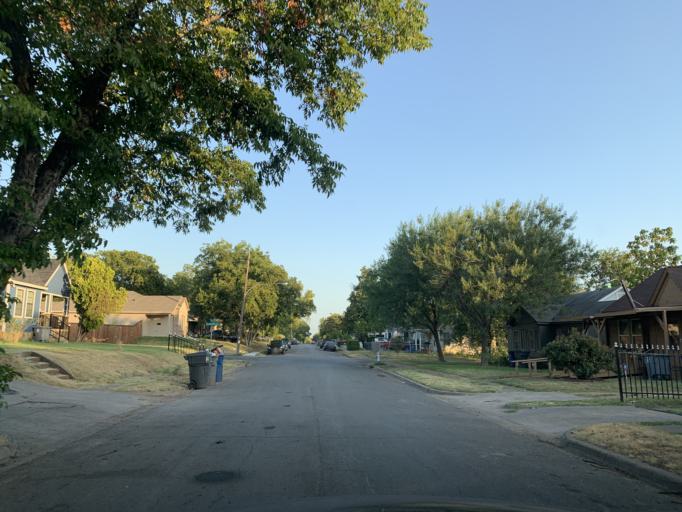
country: US
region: Texas
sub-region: Dallas County
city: Dallas
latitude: 32.7115
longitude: -96.8081
